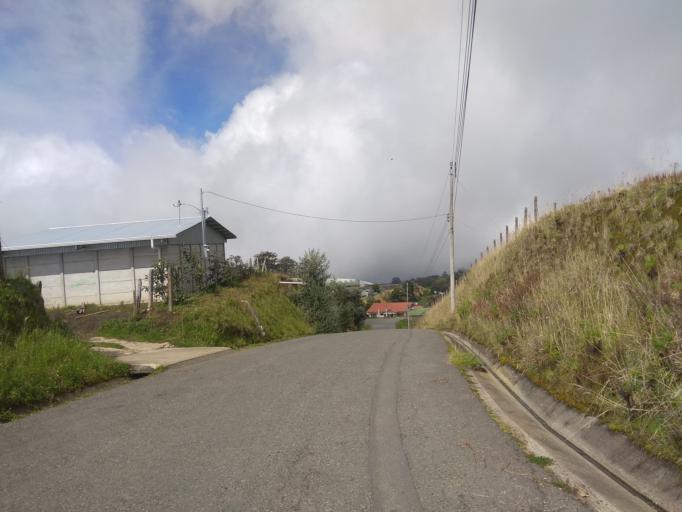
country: CR
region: Cartago
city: Cot
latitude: 9.9483
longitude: -83.9113
